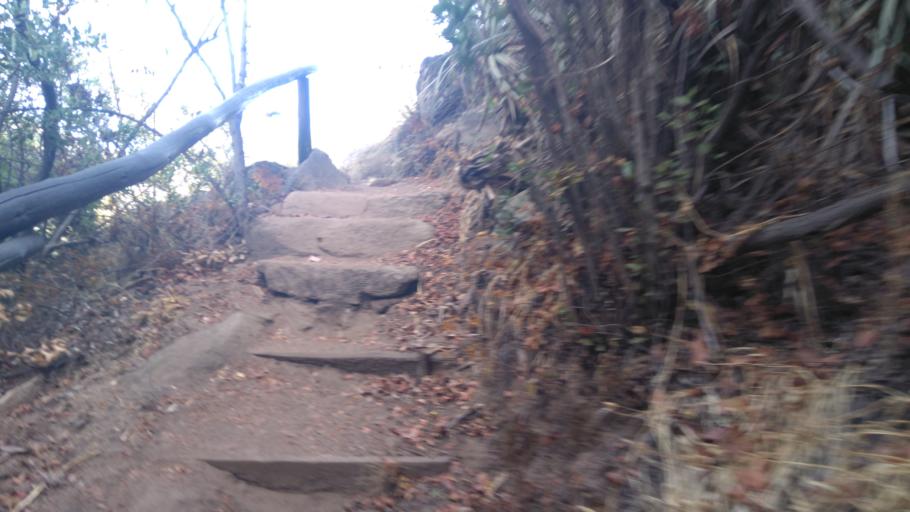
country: CL
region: Santiago Metropolitan
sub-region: Provincia de Cordillera
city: Puente Alto
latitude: -33.7225
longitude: -70.4826
